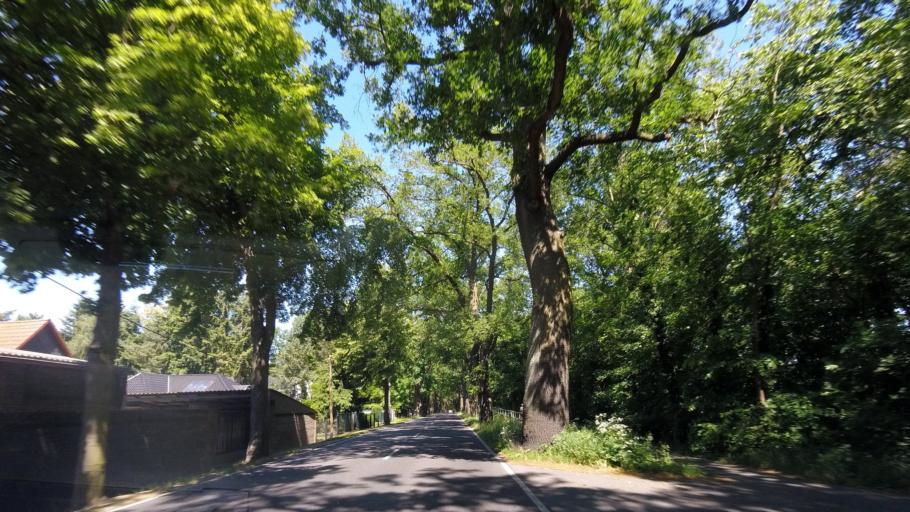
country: DE
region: Brandenburg
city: Ludwigsfelde
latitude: 52.2898
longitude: 13.2091
